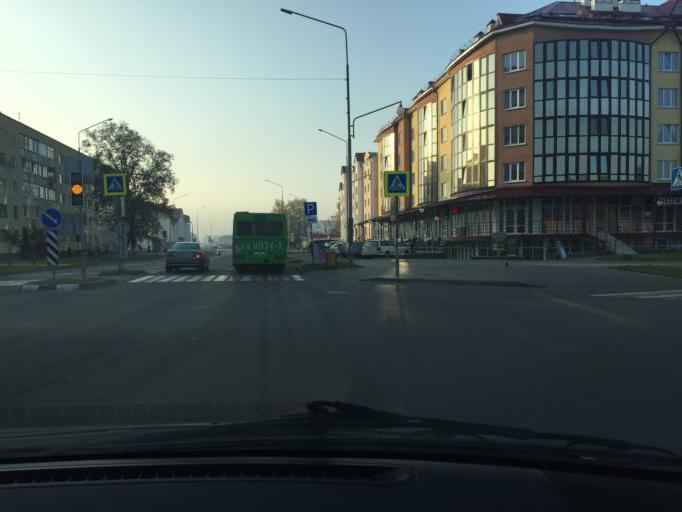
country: BY
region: Brest
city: Pinsk
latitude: 52.1198
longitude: 26.1012
